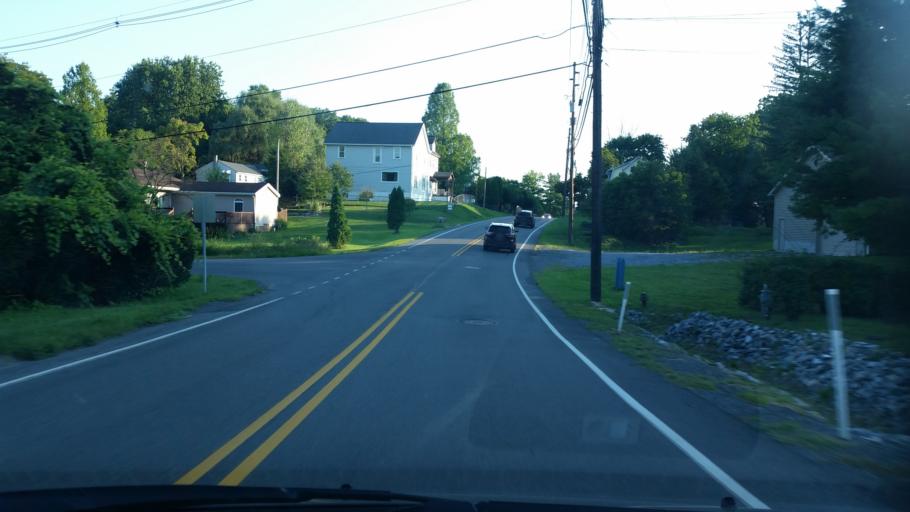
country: US
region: Pennsylvania
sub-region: Blair County
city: Altoona
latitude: 40.5451
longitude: -78.3989
